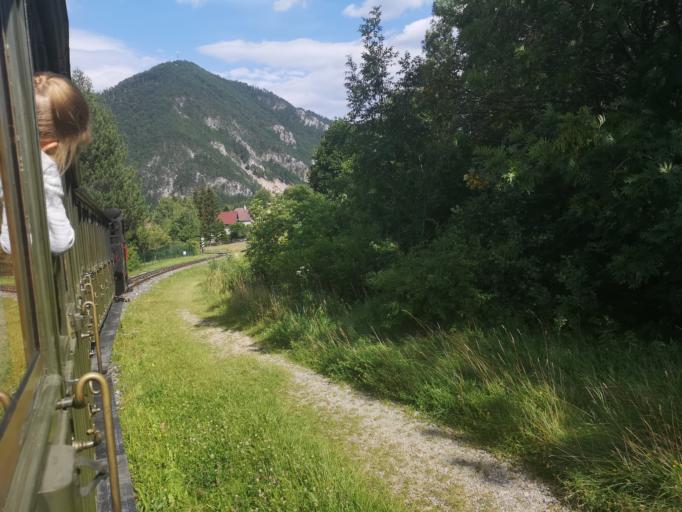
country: AT
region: Lower Austria
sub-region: Politischer Bezirk Neunkirchen
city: Puchberg am Schneeberg
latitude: 47.7890
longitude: 15.9038
